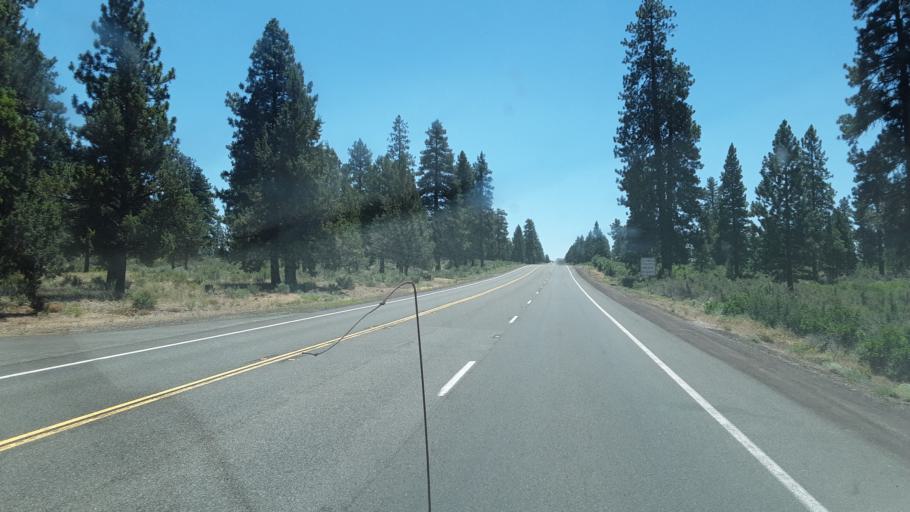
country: US
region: California
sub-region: Siskiyou County
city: Tulelake
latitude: 41.6109
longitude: -121.2122
